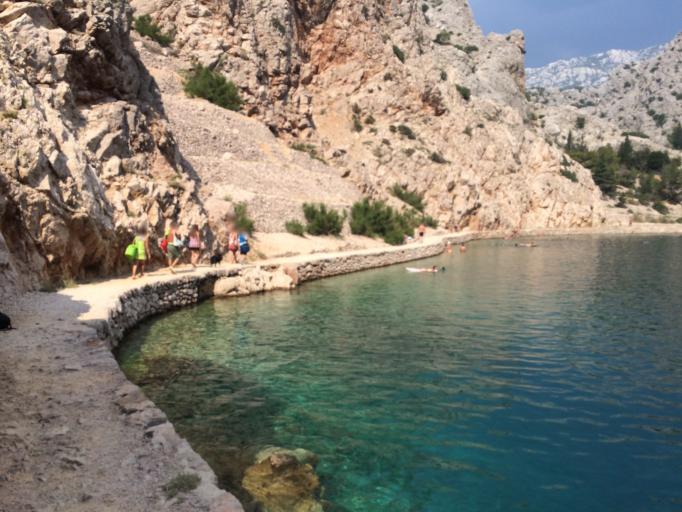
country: HR
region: Primorsko-Goranska
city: Banjol
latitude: 44.7000
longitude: 14.9006
